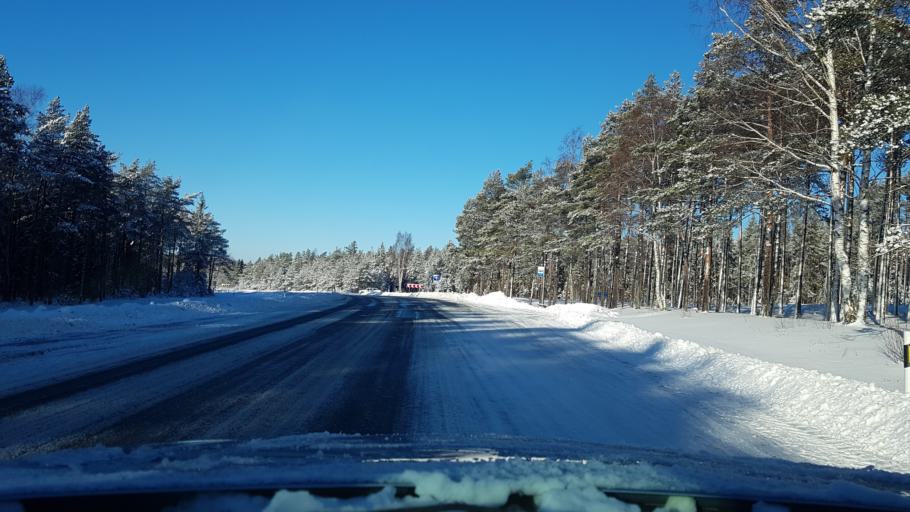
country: EE
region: Hiiumaa
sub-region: Kaerdla linn
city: Kardla
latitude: 58.9888
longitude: 22.7908
